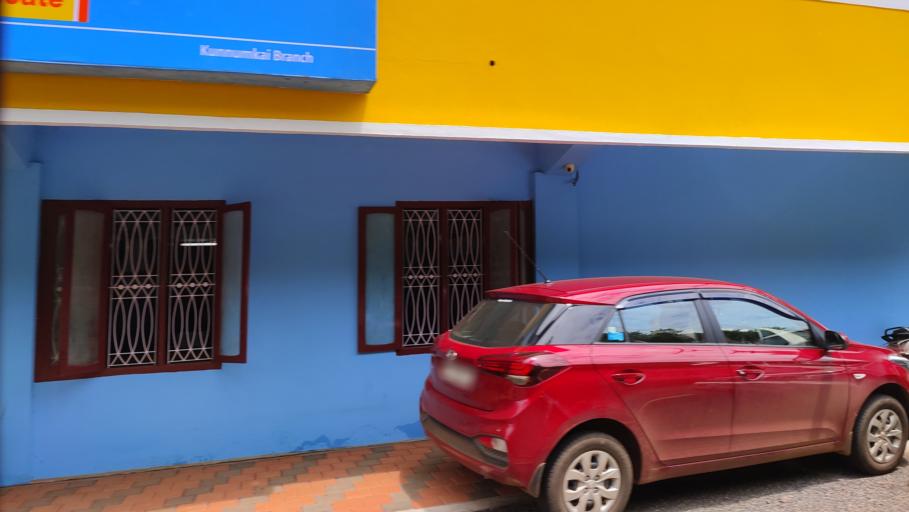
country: IN
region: Kerala
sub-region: Kasaragod District
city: Nileshwar
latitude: 12.2956
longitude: 75.2787
